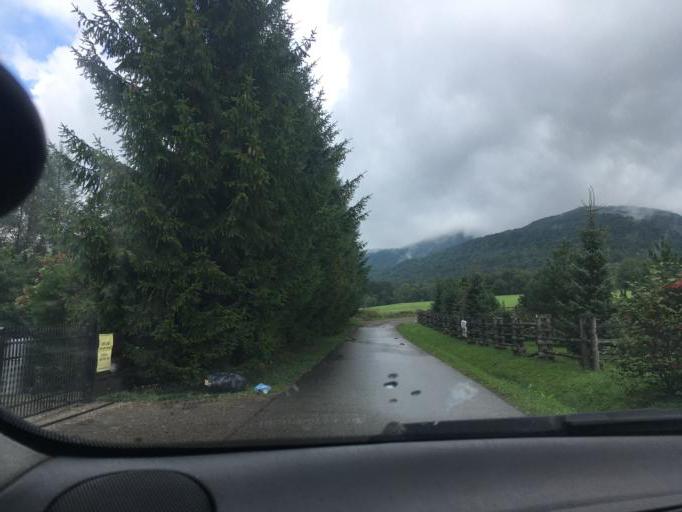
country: PL
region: Subcarpathian Voivodeship
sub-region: Powiat leski
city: Cisna
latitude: 49.1619
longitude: 22.4689
